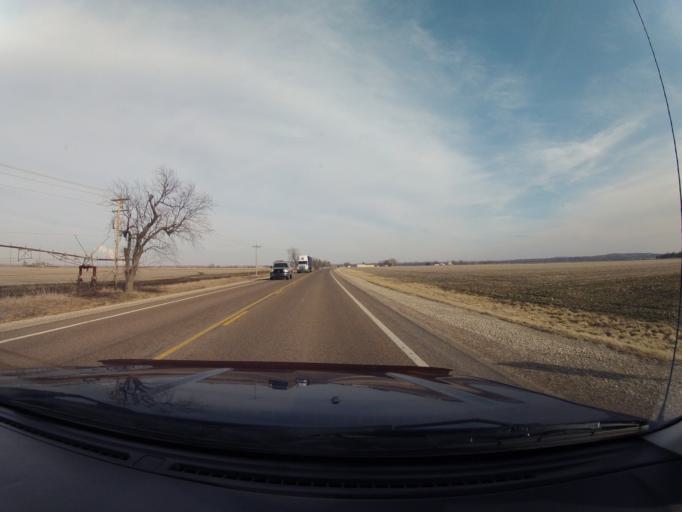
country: US
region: Kansas
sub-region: Pottawatomie County
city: Wamego
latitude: 39.2099
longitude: -96.2782
